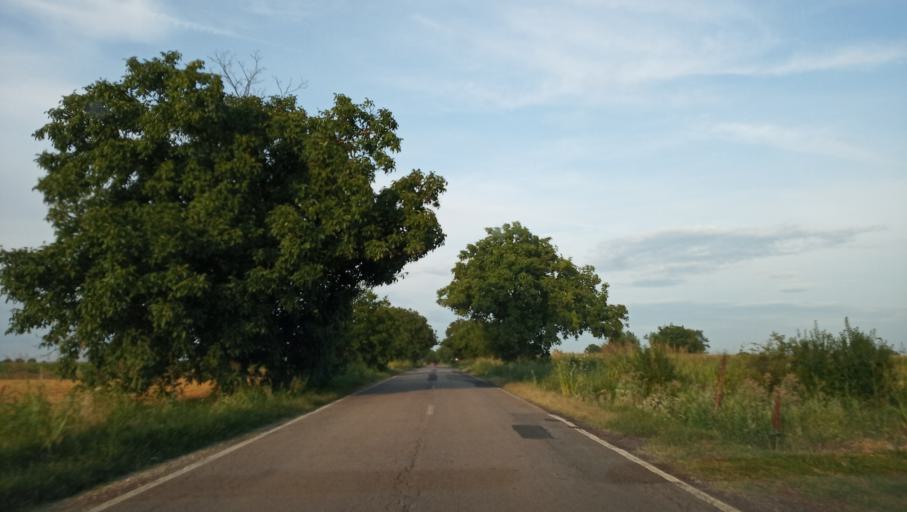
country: RO
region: Giurgiu
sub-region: Comuna Greaca
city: Greaca
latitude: 44.1055
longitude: 26.3075
